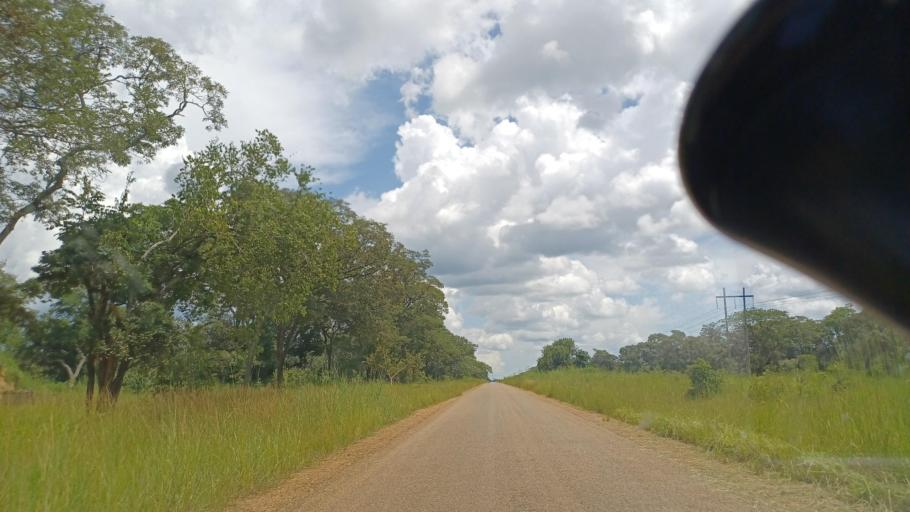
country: ZM
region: North-Western
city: Solwezi
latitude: -12.7042
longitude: 26.0325
